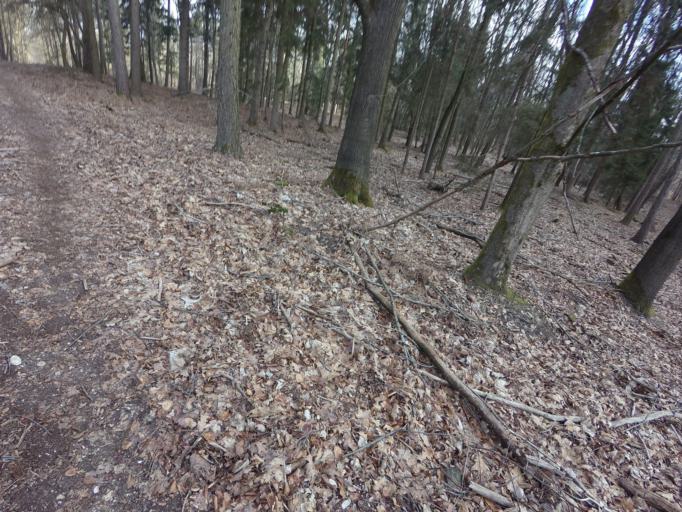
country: NL
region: Limburg
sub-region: Gemeente Roerdalen
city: Herkenbosch
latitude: 51.1740
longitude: 6.0961
